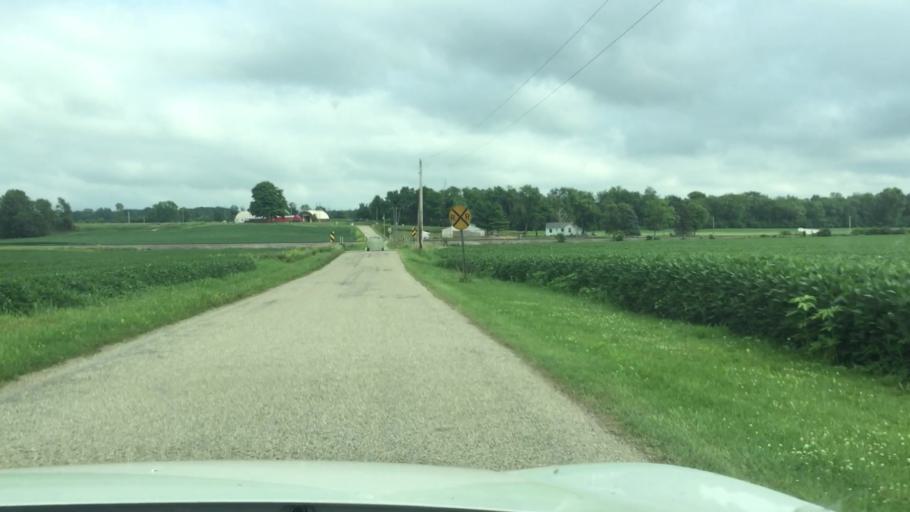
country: US
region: Ohio
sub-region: Champaign County
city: Mechanicsburg
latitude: 40.0491
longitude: -83.6346
